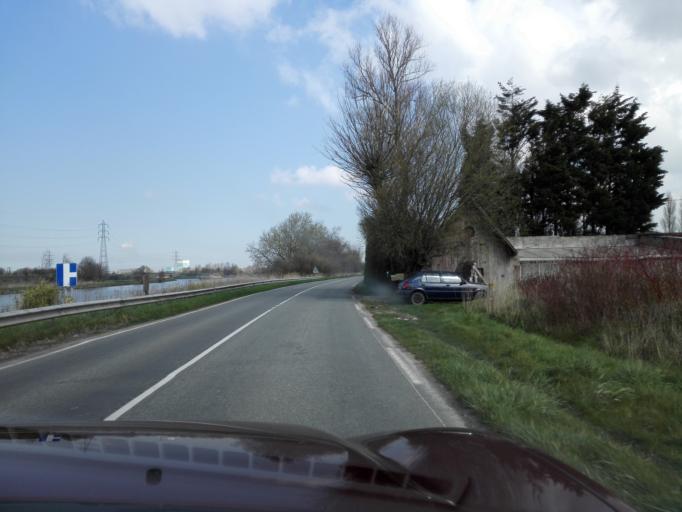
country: FR
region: Nord-Pas-de-Calais
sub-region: Departement du Nord
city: Brouckerque
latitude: 50.9684
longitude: 2.2787
